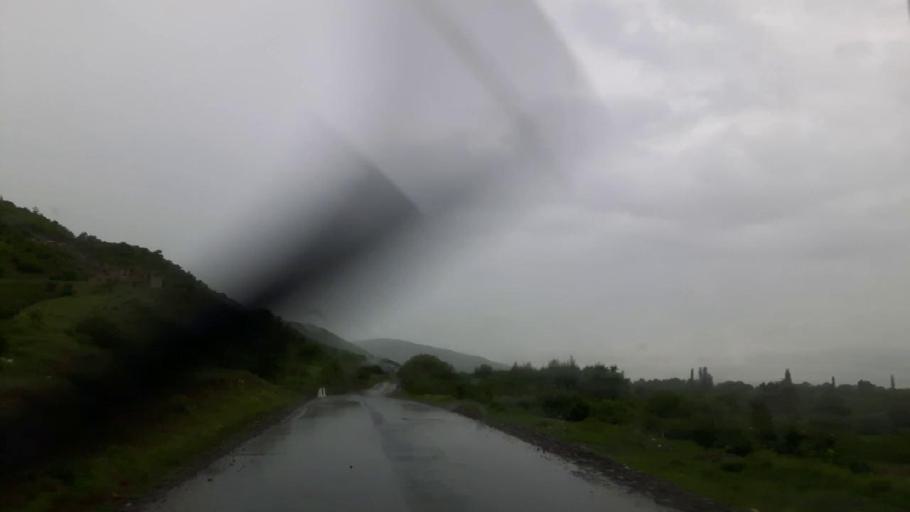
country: GE
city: Agara
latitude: 41.9841
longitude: 43.9274
